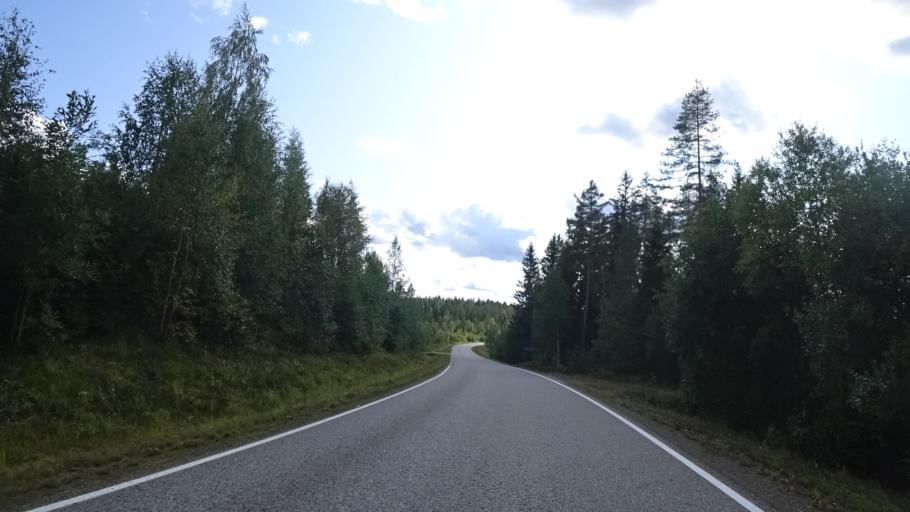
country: RU
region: Republic of Karelia
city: Vyartsilya
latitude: 62.2648
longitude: 30.7767
